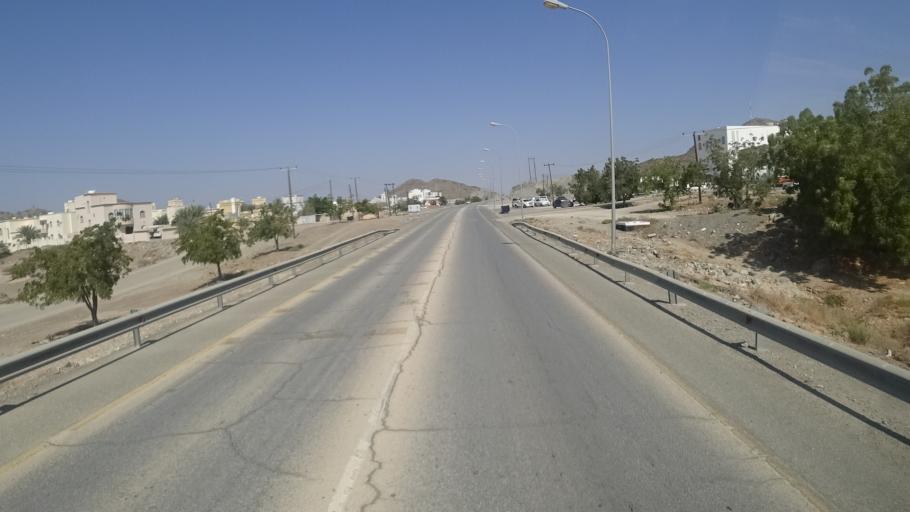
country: OM
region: Ash Sharqiyah
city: Ibra'
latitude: 22.6900
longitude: 58.5511
